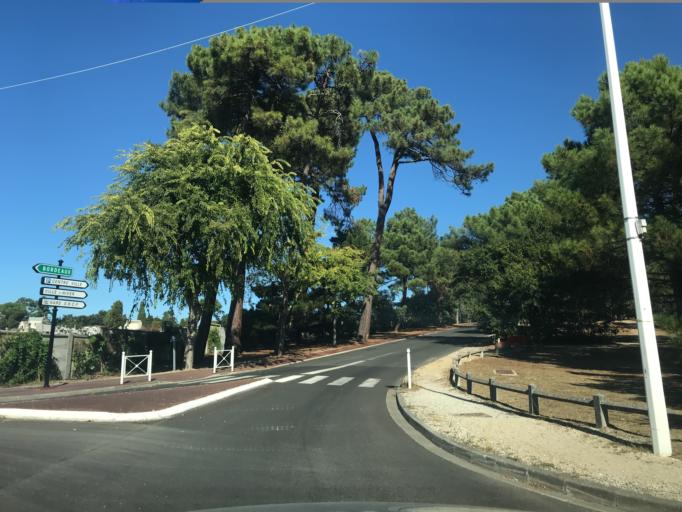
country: FR
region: Aquitaine
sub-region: Departement de la Gironde
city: Arcachon
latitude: 44.6530
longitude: -1.1809
